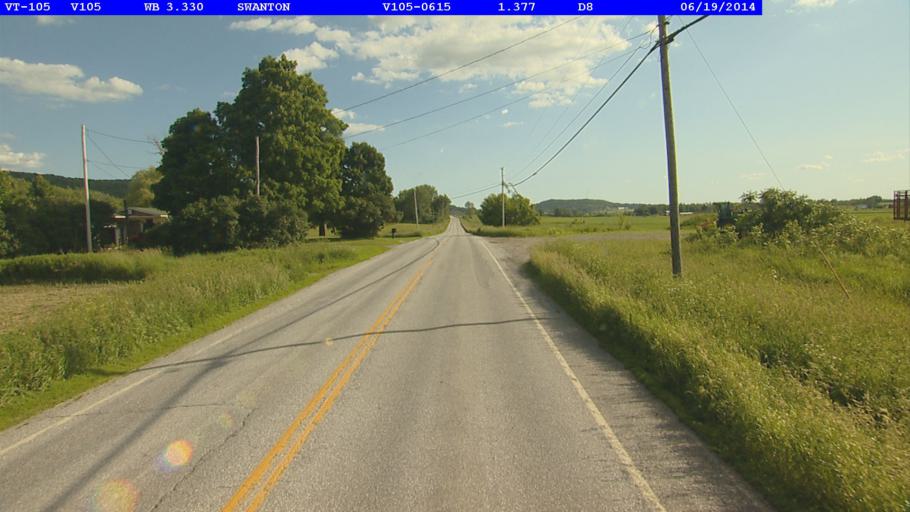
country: US
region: Vermont
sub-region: Franklin County
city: Saint Albans
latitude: 44.8526
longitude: -73.0358
